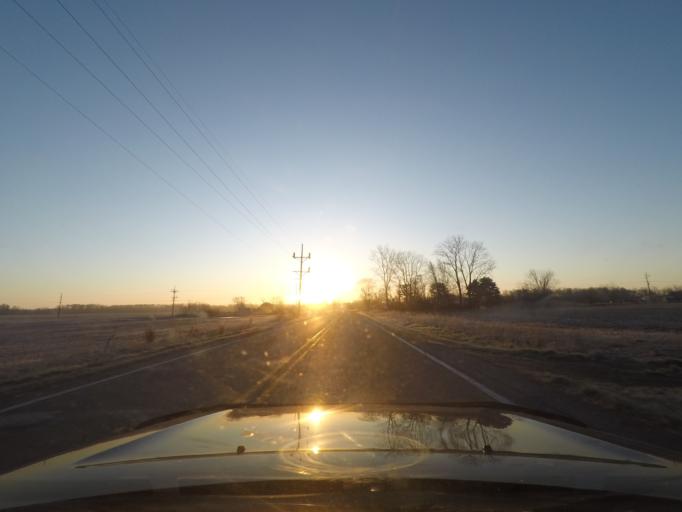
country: US
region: Indiana
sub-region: Saint Joseph County
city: Walkerton
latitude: 41.4481
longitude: -86.4080
